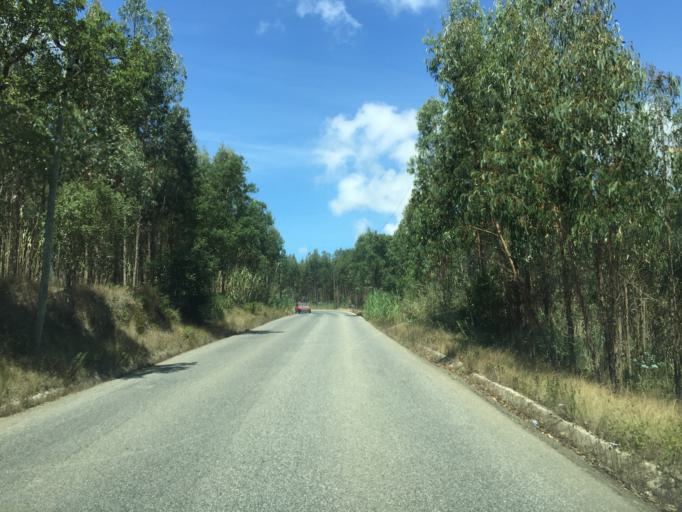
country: PT
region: Lisbon
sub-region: Lourinha
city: Lourinha
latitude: 39.2716
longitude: -9.2905
